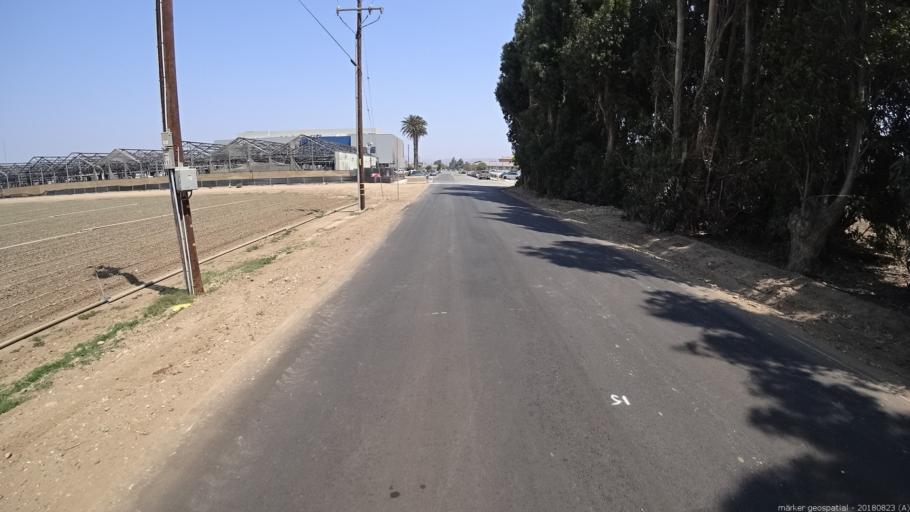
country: US
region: California
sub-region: Monterey County
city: Greenfield
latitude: 36.3286
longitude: -121.2533
